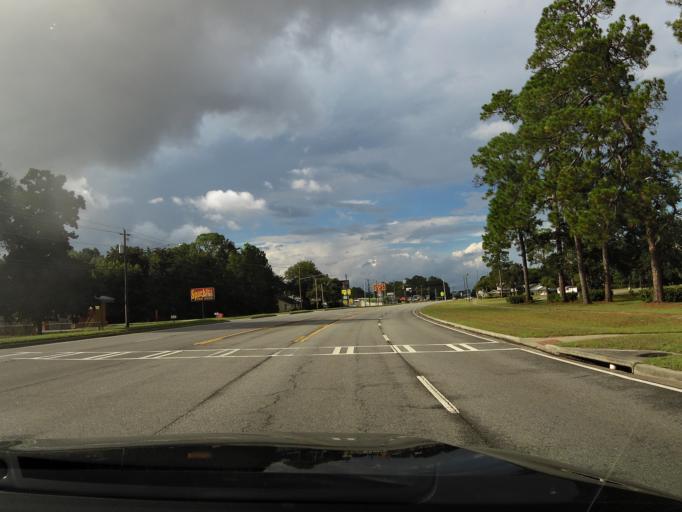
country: US
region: Georgia
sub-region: Liberty County
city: Hinesville
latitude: 31.8486
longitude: -81.6056
